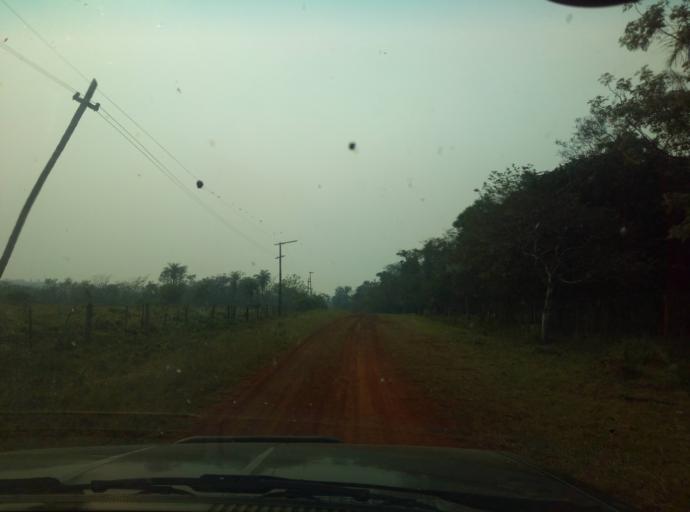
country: PY
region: Caaguazu
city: Carayao
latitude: -25.2037
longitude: -56.2277
